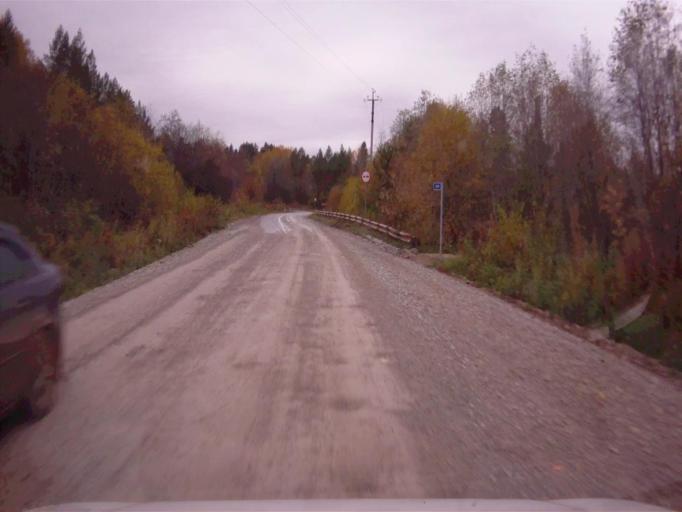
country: RU
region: Chelyabinsk
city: Nyazepetrovsk
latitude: 56.0500
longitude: 59.4954
